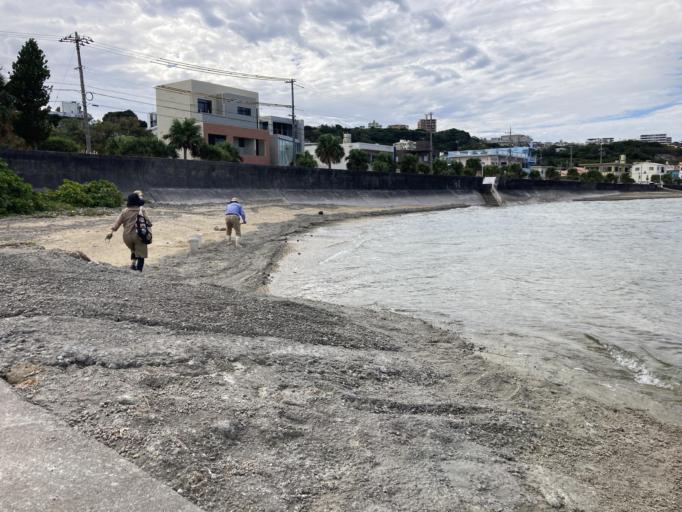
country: JP
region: Okinawa
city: Ishikawa
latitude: 26.4227
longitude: 127.7406
